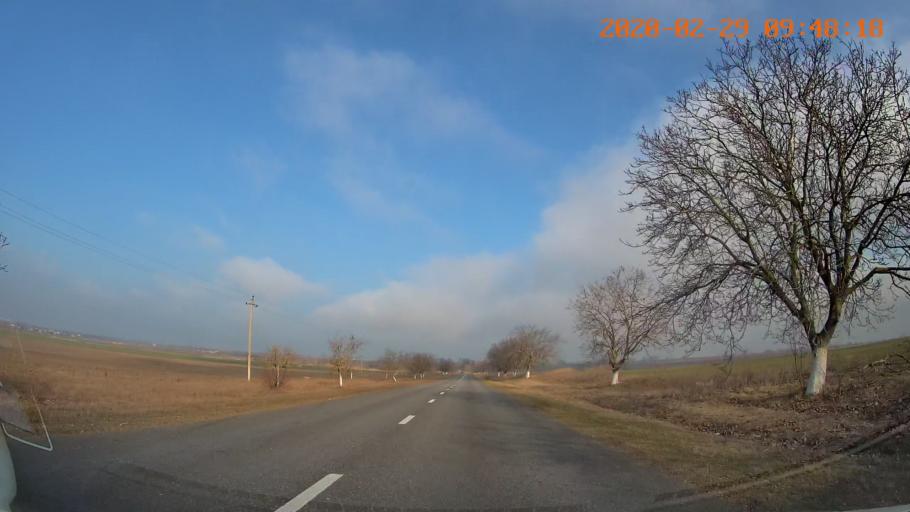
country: MD
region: Telenesti
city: Crasnoe
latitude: 46.6866
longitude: 29.7854
